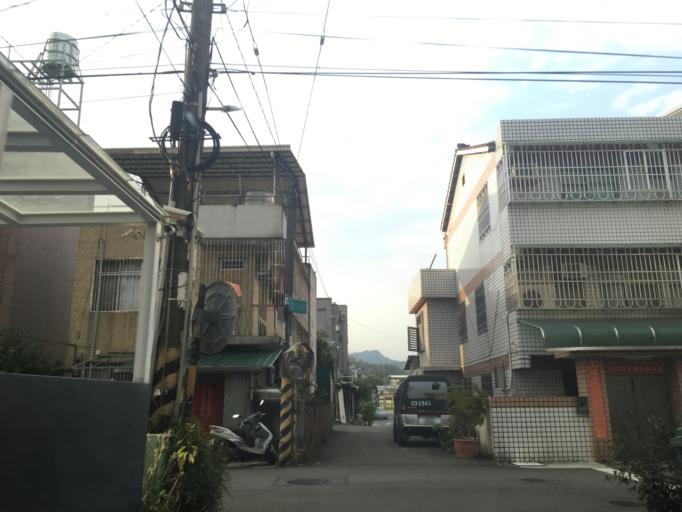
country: TW
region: Taiwan
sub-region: Taichung City
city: Taichung
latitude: 24.1726
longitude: 120.7324
